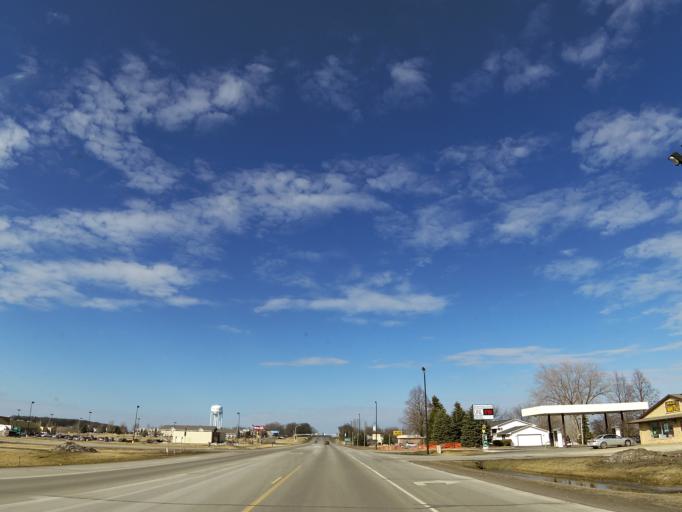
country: US
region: Minnesota
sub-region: Waseca County
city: Waseca
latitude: 44.0951
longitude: -93.5071
